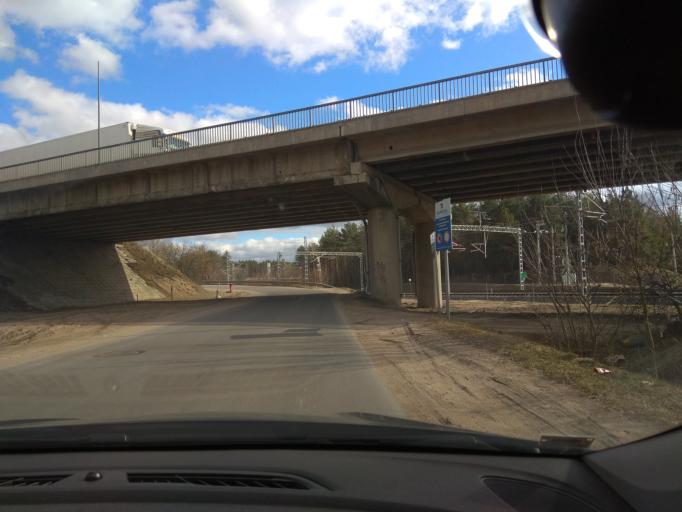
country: LT
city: Baltoji Voke
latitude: 54.6318
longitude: 25.1455
